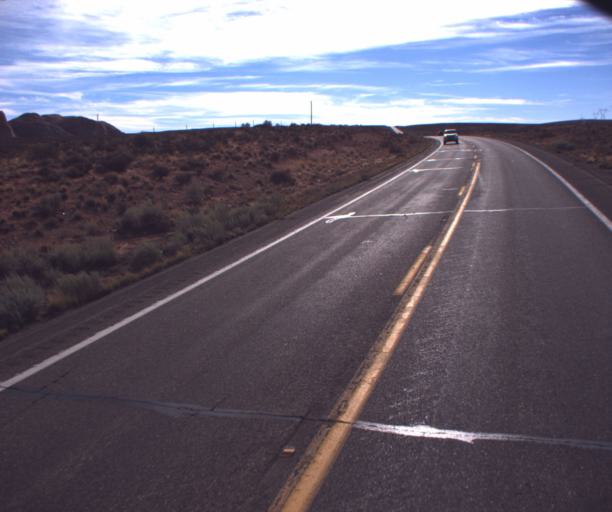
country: US
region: Arizona
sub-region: Coconino County
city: LeChee
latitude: 36.8438
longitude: -111.3288
